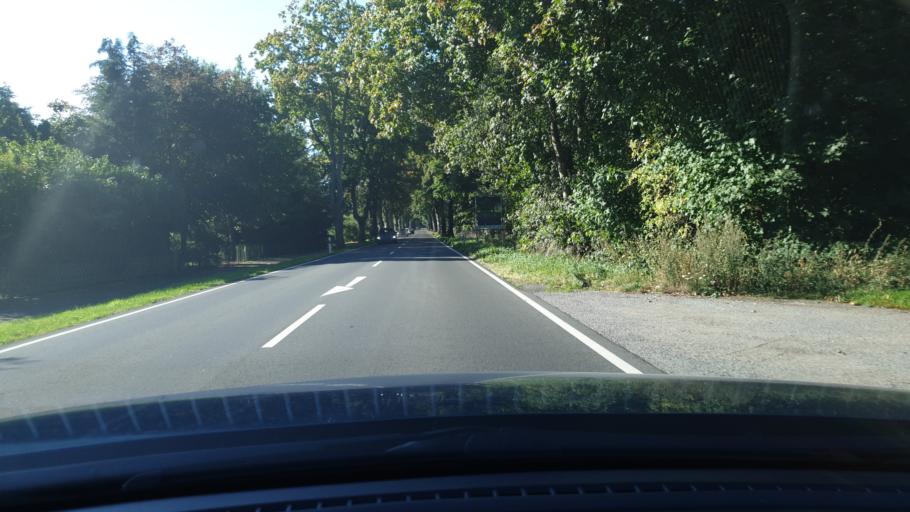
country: DE
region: Mecklenburg-Vorpommern
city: Lutzow
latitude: 53.6437
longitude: 11.1664
